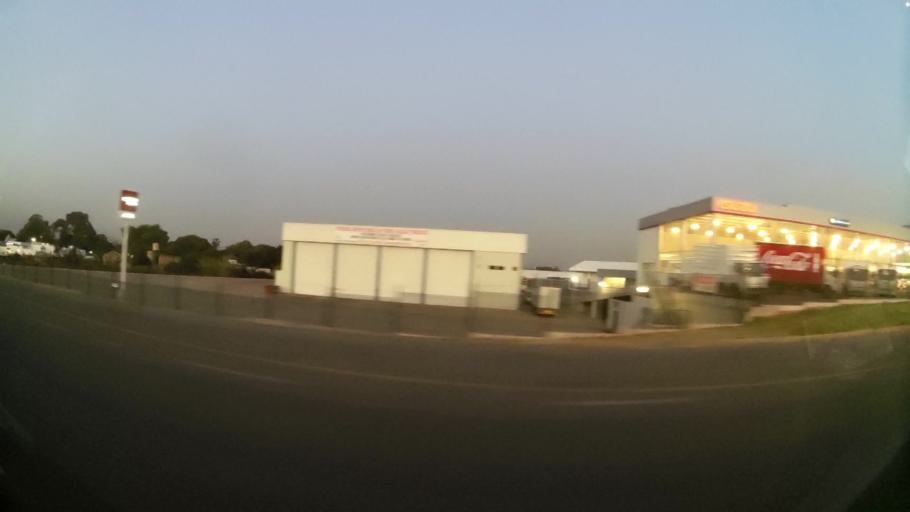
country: ZA
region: North-West
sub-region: Bojanala Platinum District Municipality
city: Rustenburg
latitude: -25.6843
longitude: 27.2548
